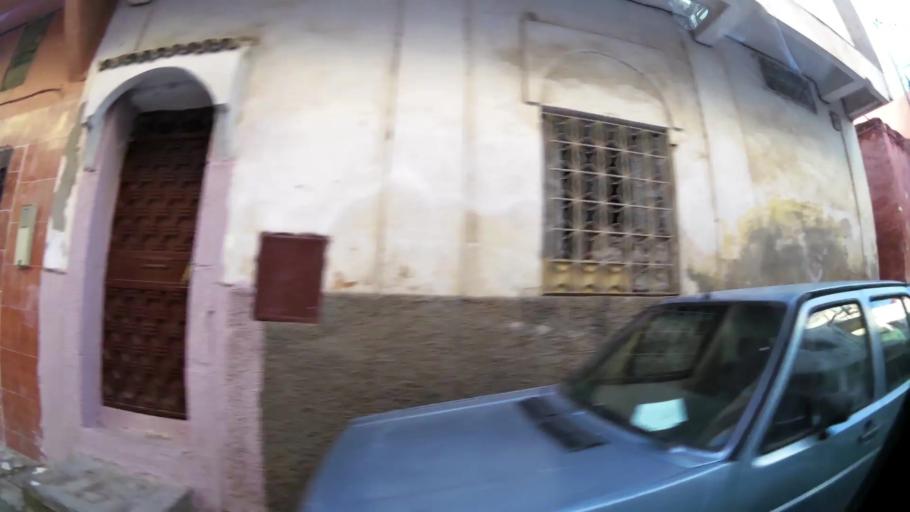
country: MA
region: Chaouia-Ouardigha
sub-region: Settat Province
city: Settat
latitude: 33.0042
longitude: -7.6243
